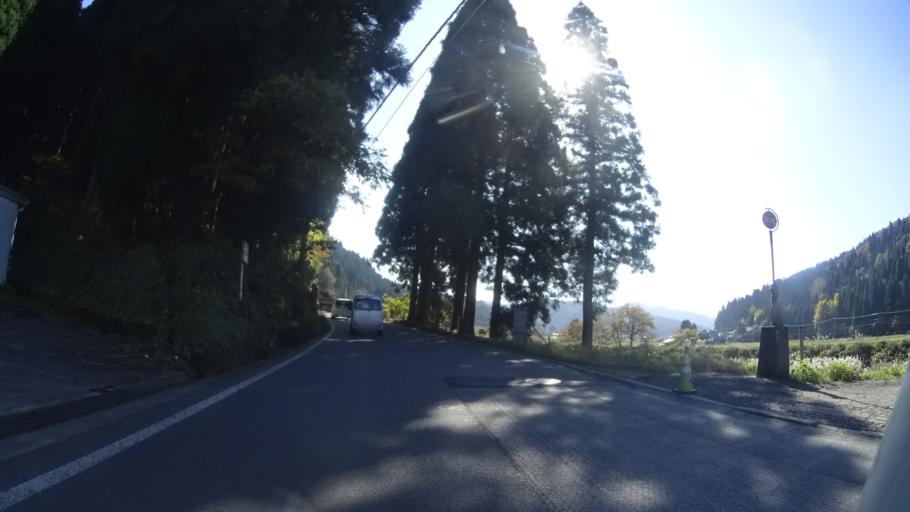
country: JP
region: Fukui
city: Ono
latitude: 35.9116
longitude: 136.3552
